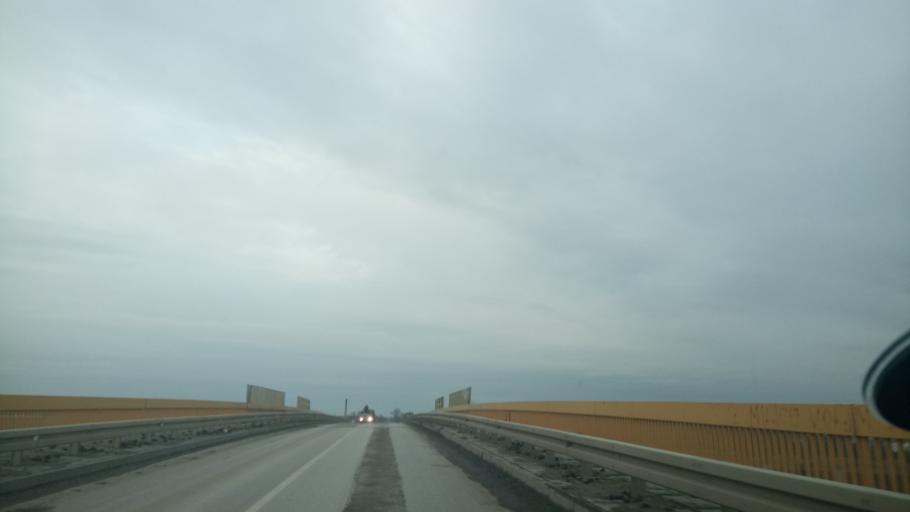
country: RS
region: Autonomna Pokrajina Vojvodina
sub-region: Sremski Okrug
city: Stara Pazova
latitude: 44.9652
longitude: 20.1611
